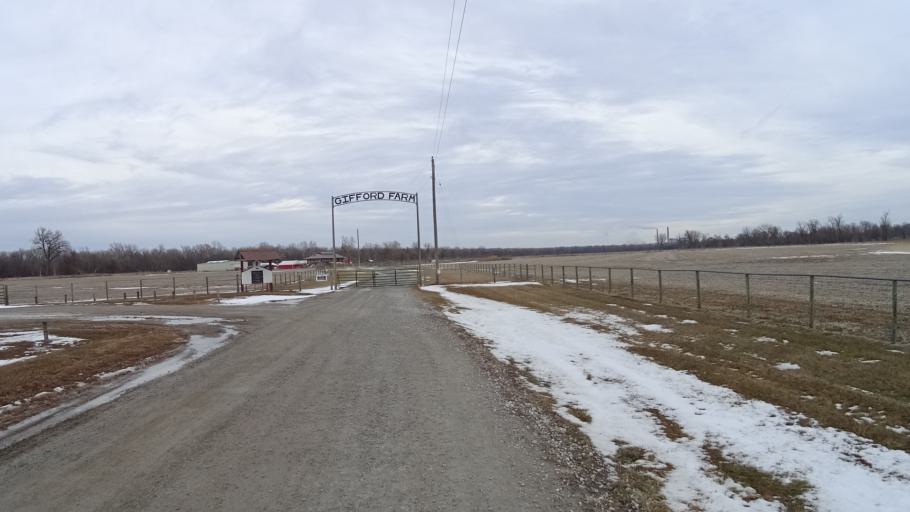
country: US
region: Nebraska
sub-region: Sarpy County
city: Bellevue
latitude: 41.1754
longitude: -95.8895
